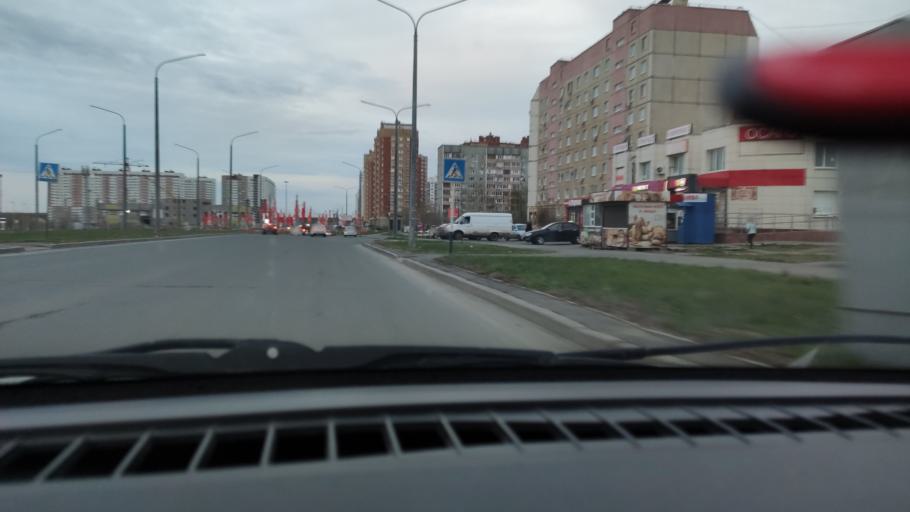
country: RU
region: Orenburg
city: Orenburg
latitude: 51.8233
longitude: 55.1640
